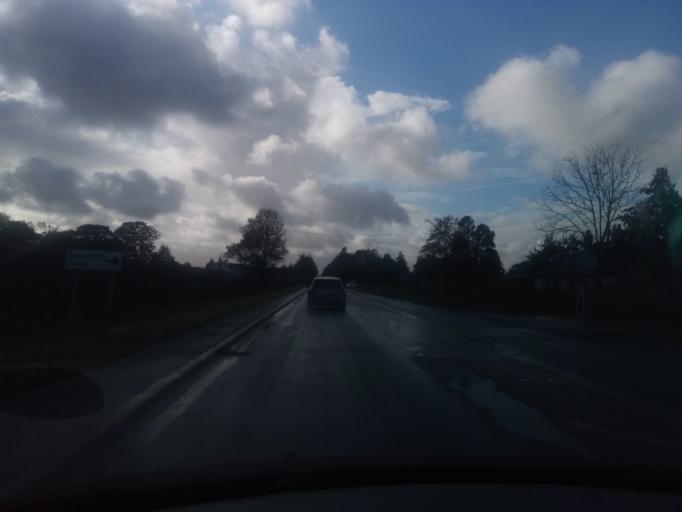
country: GB
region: England
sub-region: Cumbria
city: Carlisle
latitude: 54.9405
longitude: -2.9442
